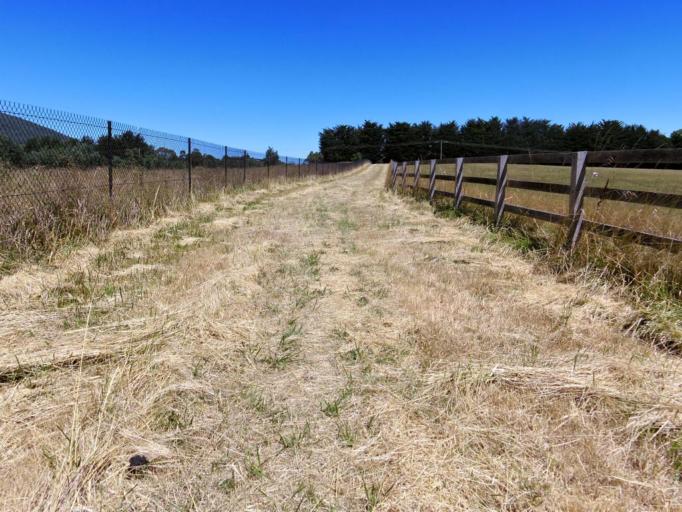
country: AU
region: Victoria
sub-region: Hume
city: Sunbury
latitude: -37.3535
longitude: 144.5495
